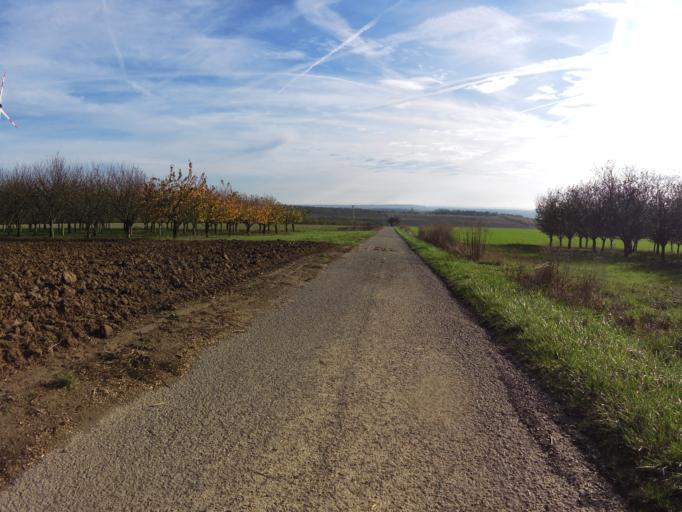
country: DE
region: Bavaria
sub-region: Regierungsbezirk Unterfranken
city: Sommerhausen
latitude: 49.7162
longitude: 10.0386
